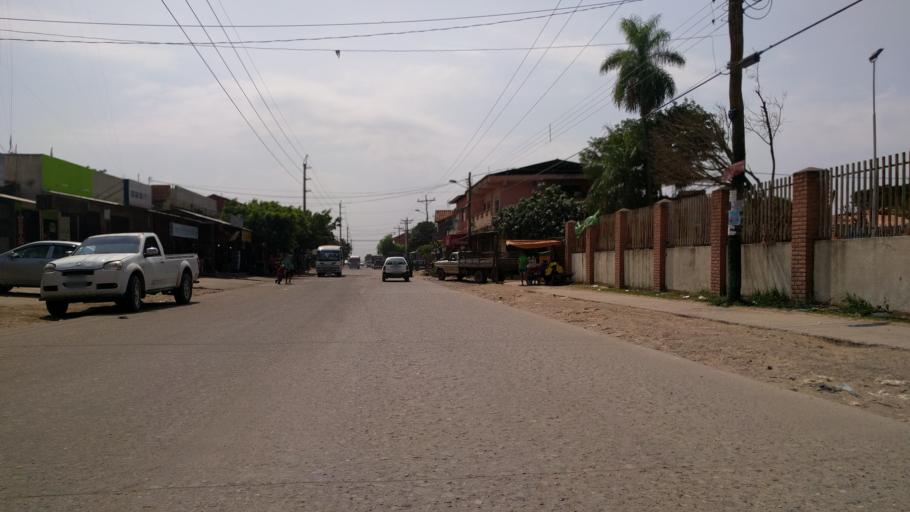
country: BO
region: Santa Cruz
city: Santa Cruz de la Sierra
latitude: -17.8449
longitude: -63.2147
